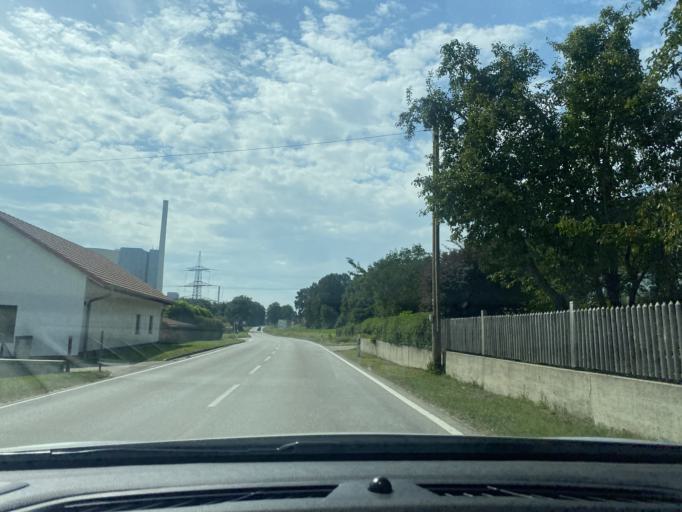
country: DE
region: Bavaria
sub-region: Upper Bavaria
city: Haag an der Amper
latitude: 48.4578
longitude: 11.8120
